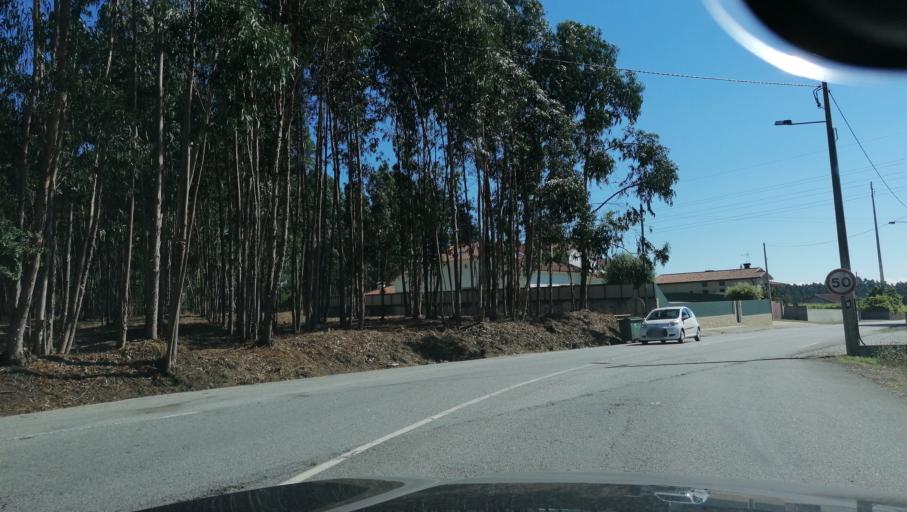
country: PT
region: Aveiro
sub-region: Estarreja
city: Beduido
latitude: 40.7817
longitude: -8.5505
